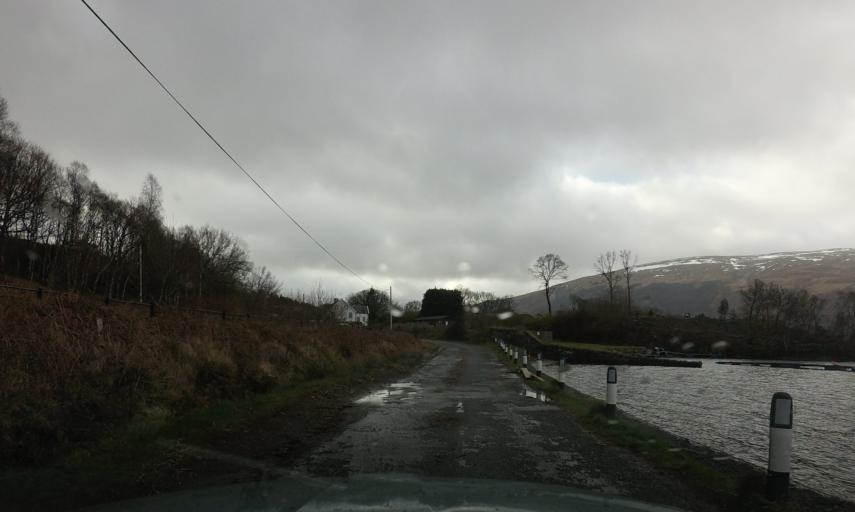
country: GB
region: Scotland
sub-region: West Dunbartonshire
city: Balloch
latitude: 56.1509
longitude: -4.6417
